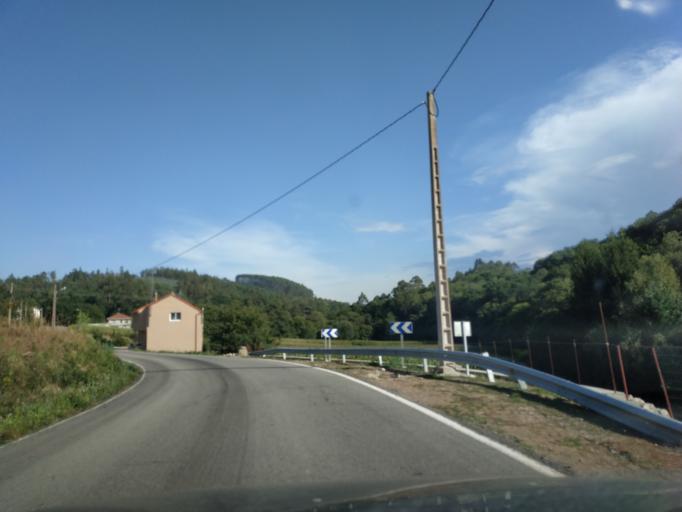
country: ES
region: Galicia
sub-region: Provincia da Coruna
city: Cerceda
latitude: 43.2329
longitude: -8.4792
